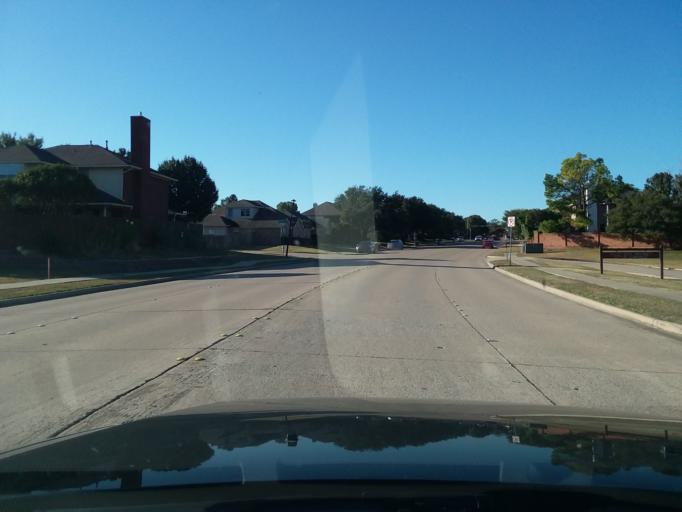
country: US
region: Texas
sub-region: Denton County
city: Lewisville
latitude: 33.0544
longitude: -97.0237
